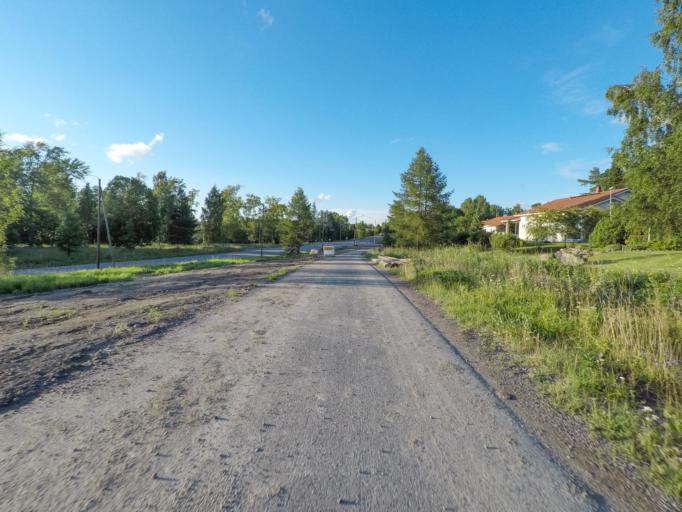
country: FI
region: South Karelia
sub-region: Imatra
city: Imatra
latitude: 61.2006
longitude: 28.7853
